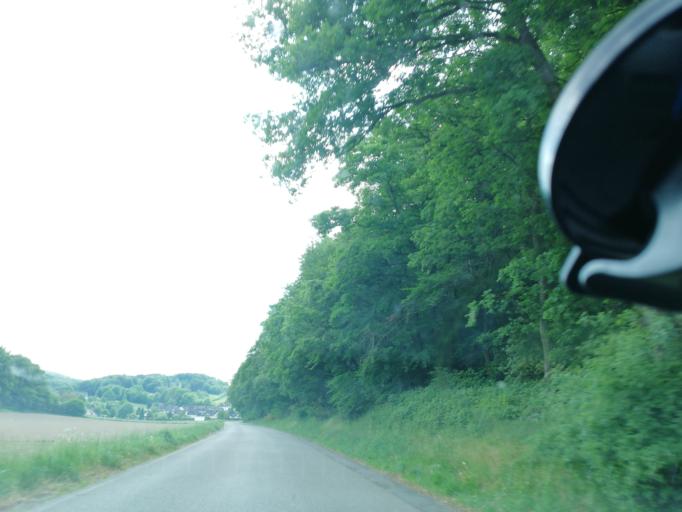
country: DE
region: North Rhine-Westphalia
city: Wetter (Ruhr)
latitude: 51.3768
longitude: 7.3402
